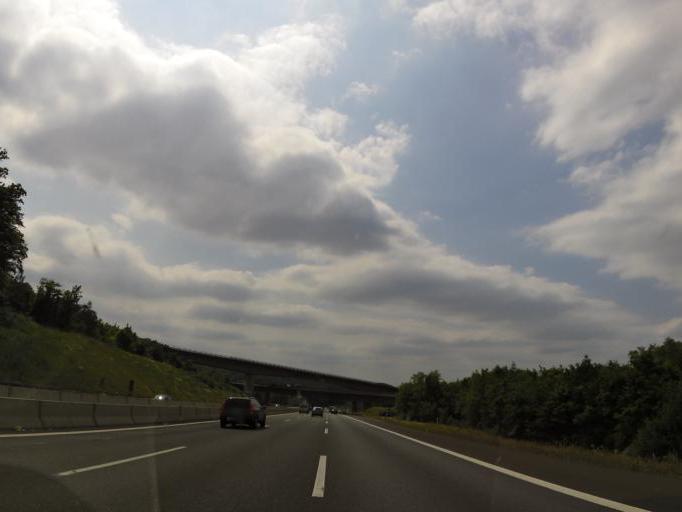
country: DE
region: Bavaria
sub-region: Regierungsbezirk Unterfranken
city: Eisingen
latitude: 49.7483
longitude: 9.8218
